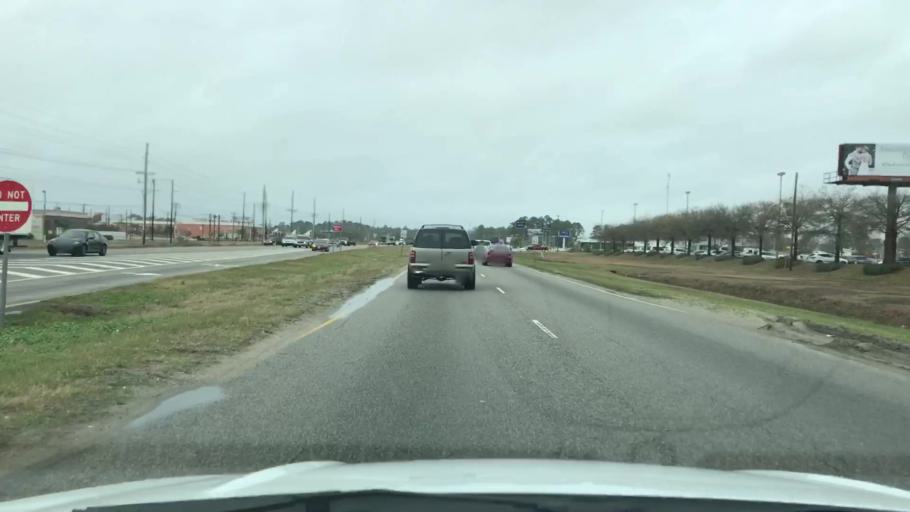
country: US
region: South Carolina
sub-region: Horry County
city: Red Hill
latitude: 33.7910
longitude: -78.9970
